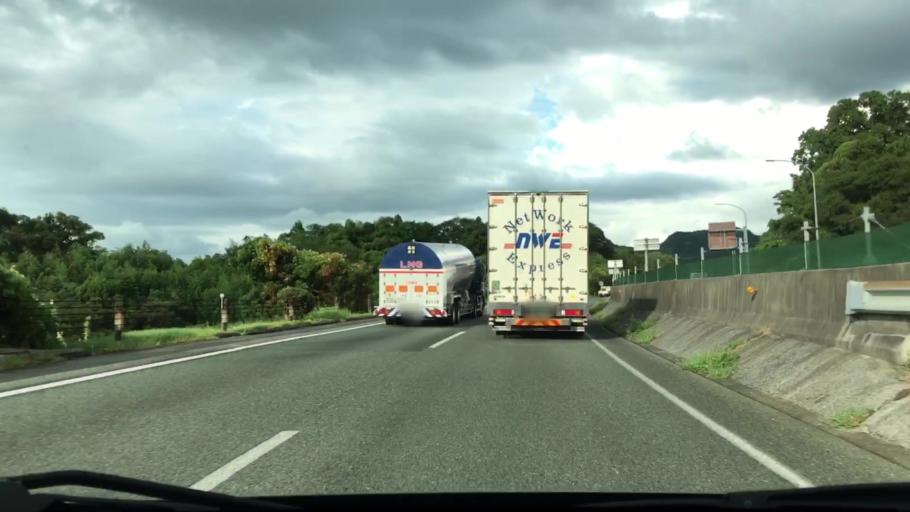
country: JP
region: Fukuoka
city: Nishifukuma
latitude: 33.7488
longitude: 130.5306
